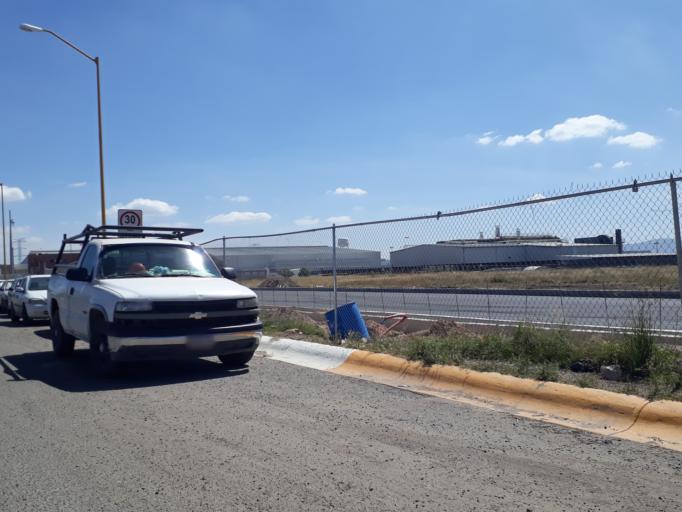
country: MX
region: Aguascalientes
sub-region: Aguascalientes
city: San Sebastian [Fraccionamiento]
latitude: 21.7996
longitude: -102.2957
